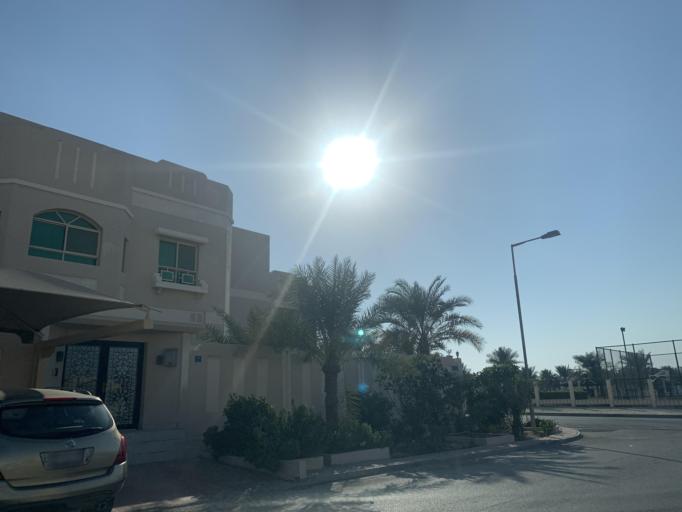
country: BH
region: Central Governorate
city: Madinat Hamad
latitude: 26.1072
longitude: 50.5092
